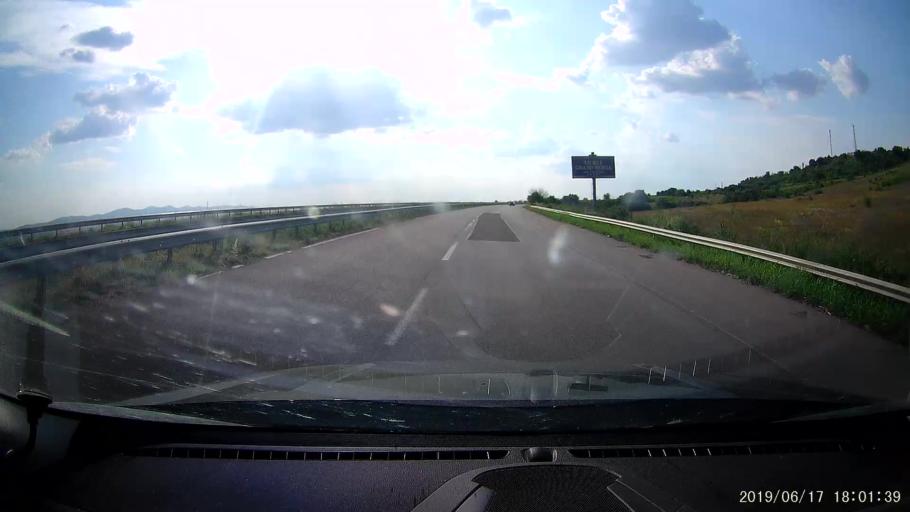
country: BG
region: Khaskovo
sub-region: Obshtina Svilengrad
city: Svilengrad
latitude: 41.7471
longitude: 26.2480
